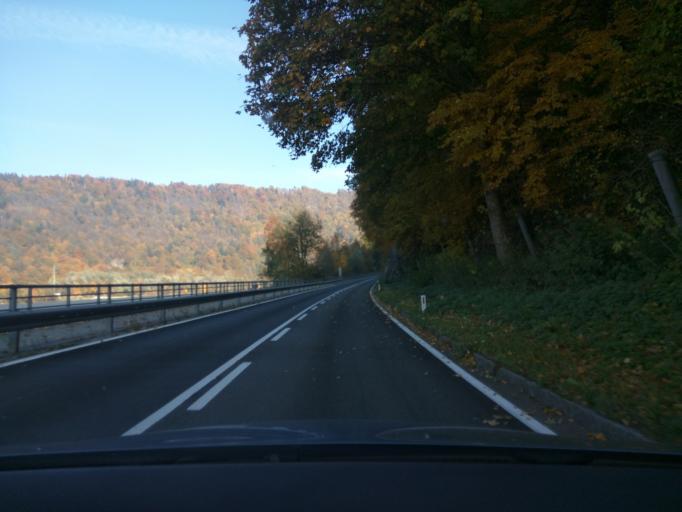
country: DE
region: Bavaria
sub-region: Lower Bavaria
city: Obernzell
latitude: 48.5630
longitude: 13.5858
